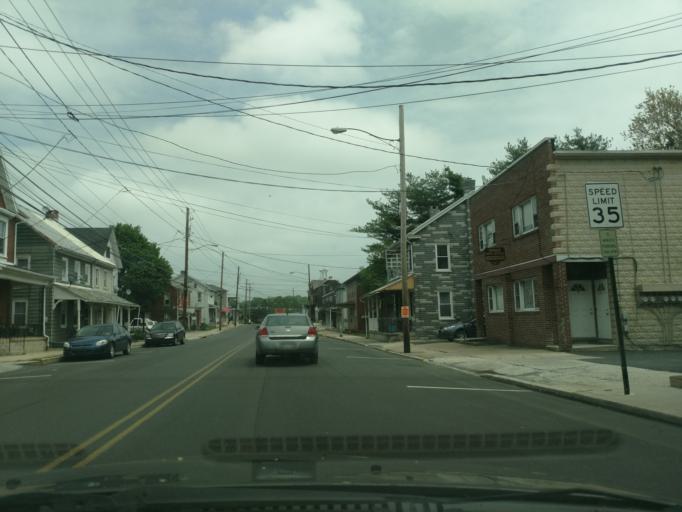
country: US
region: Pennsylvania
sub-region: Berks County
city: Sinking Spring
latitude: 40.3251
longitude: -76.0232
